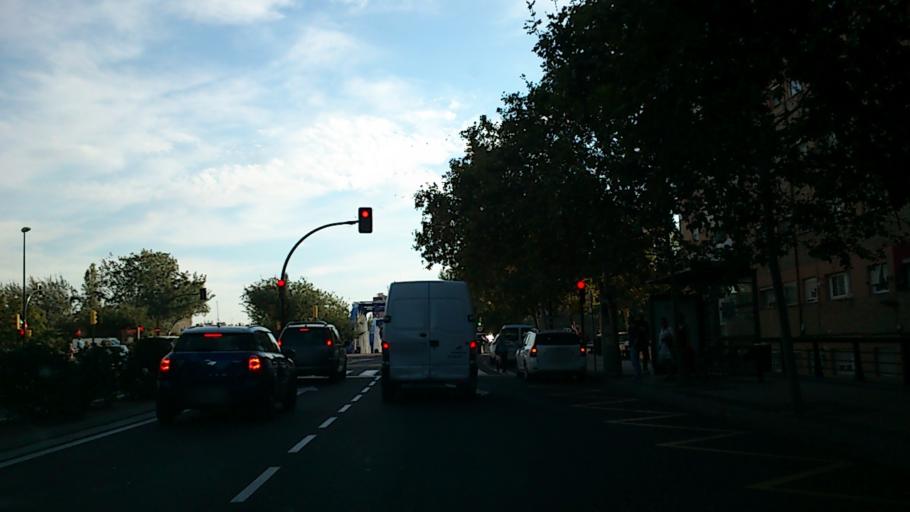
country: ES
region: Aragon
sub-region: Provincia de Zaragoza
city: Zaragoza
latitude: 41.6572
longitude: -0.8697
